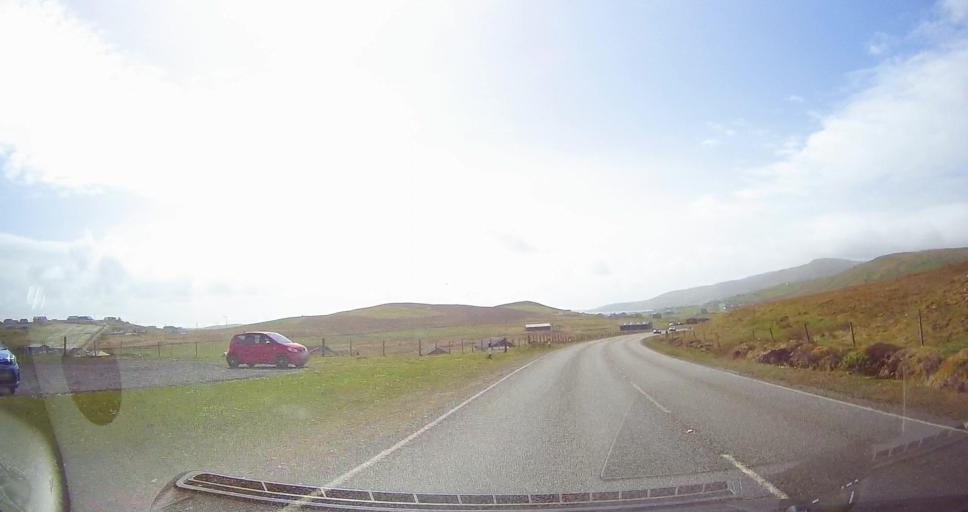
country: GB
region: Scotland
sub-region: Shetland Islands
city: Sandwick
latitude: 60.0629
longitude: -1.2213
